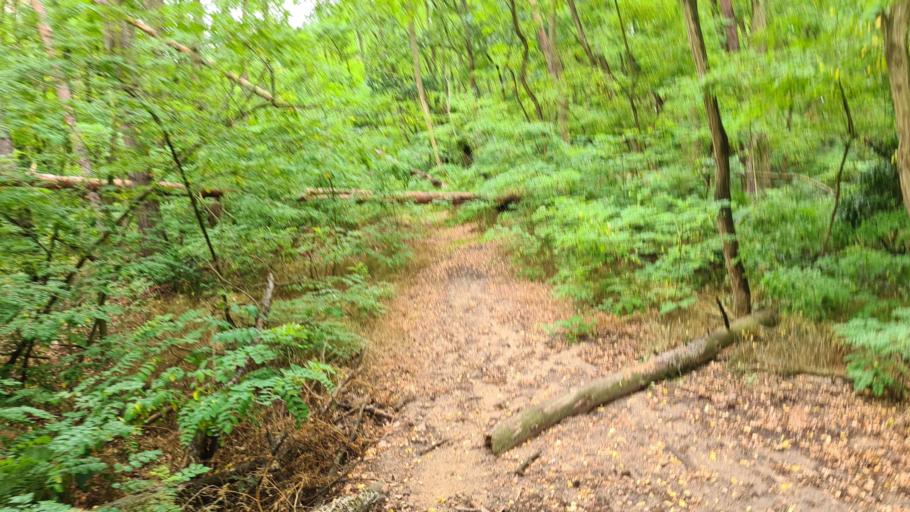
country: DE
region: Brandenburg
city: Trebbin
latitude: 52.2495
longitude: 13.1824
